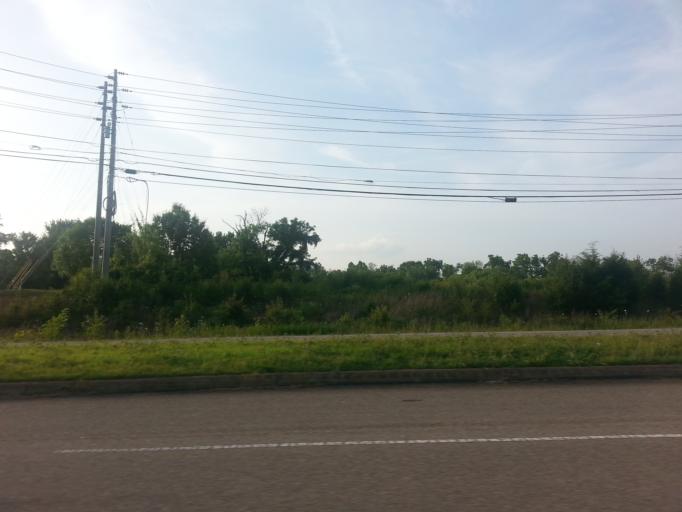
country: US
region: Tennessee
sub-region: Knox County
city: Farragut
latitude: 35.9568
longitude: -84.1316
